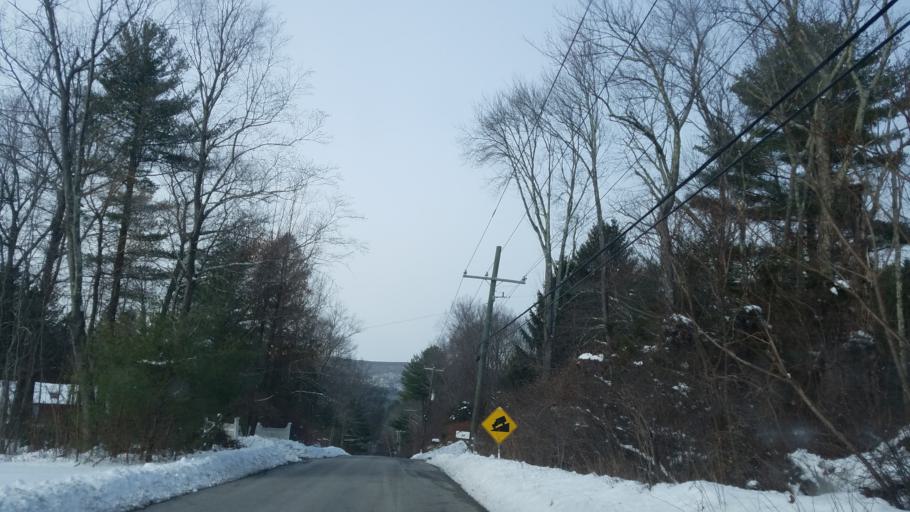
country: US
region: Connecticut
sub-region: Hartford County
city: Collinsville
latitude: 41.8400
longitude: -72.9212
